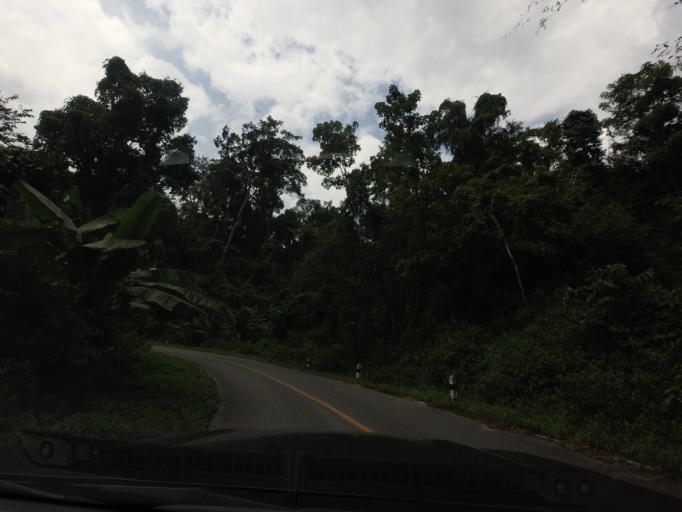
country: TH
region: Loei
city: Na Haeo
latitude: 17.7065
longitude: 100.9498
